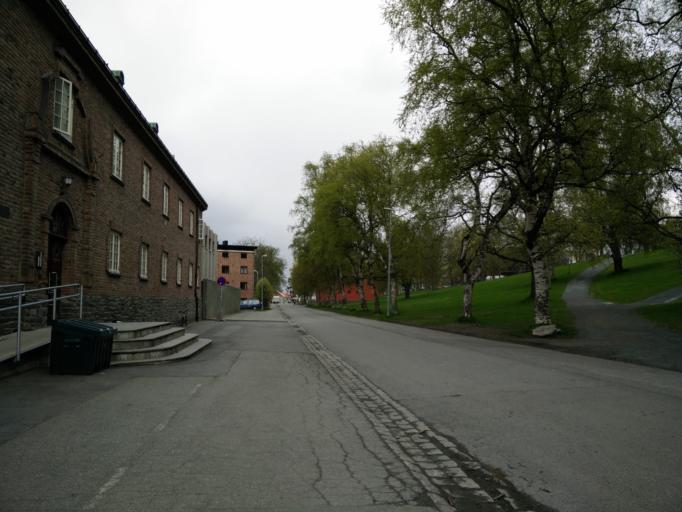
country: NO
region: Sor-Trondelag
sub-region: Trondheim
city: Trondheim
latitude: 63.4197
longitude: 10.3978
